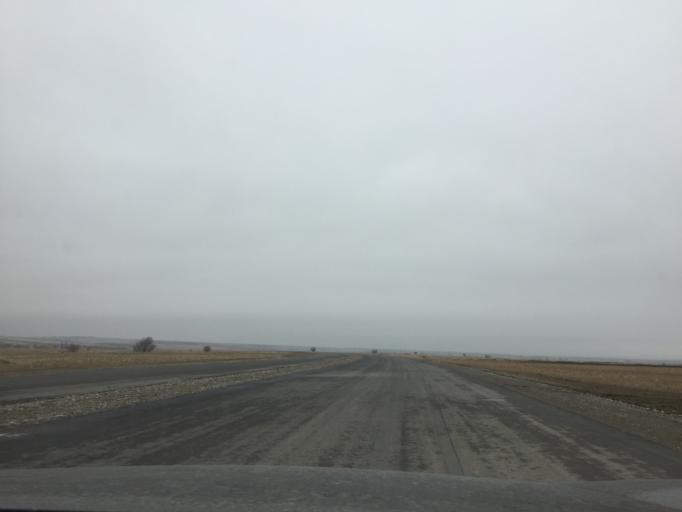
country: KZ
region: Ongtustik Qazaqstan
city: Turar Ryskulov
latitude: 42.5184
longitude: 70.3255
